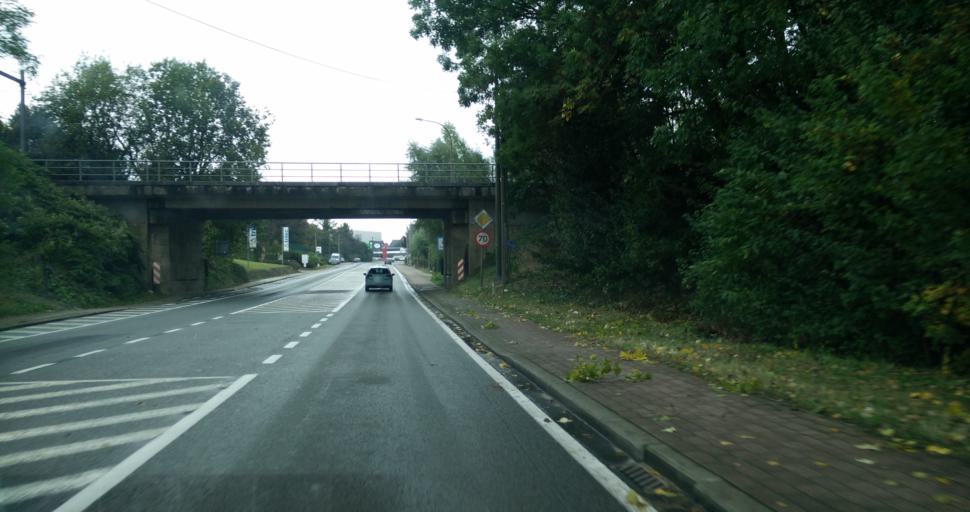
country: BE
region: Flanders
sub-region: Provincie Vlaams-Brabant
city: Halle
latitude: 50.7268
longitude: 4.2288
